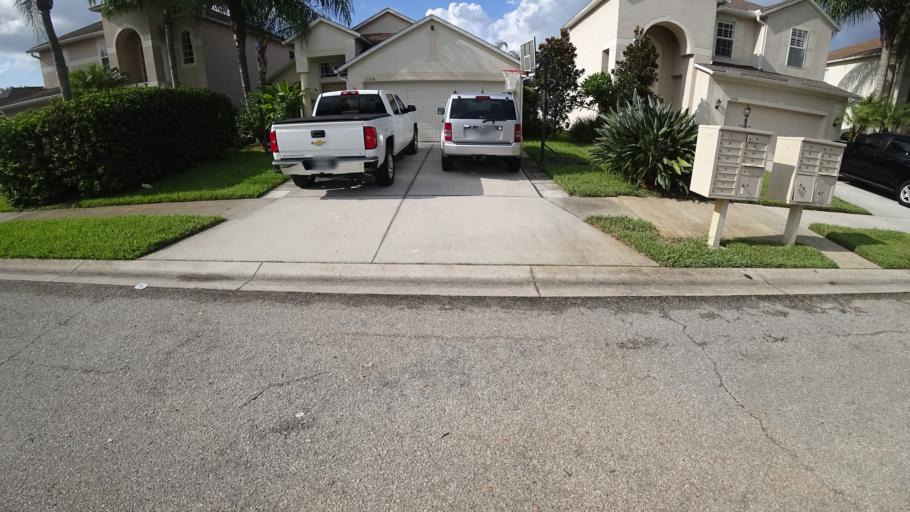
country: US
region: Florida
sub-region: Sarasota County
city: The Meadows
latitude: 27.4291
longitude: -82.4305
